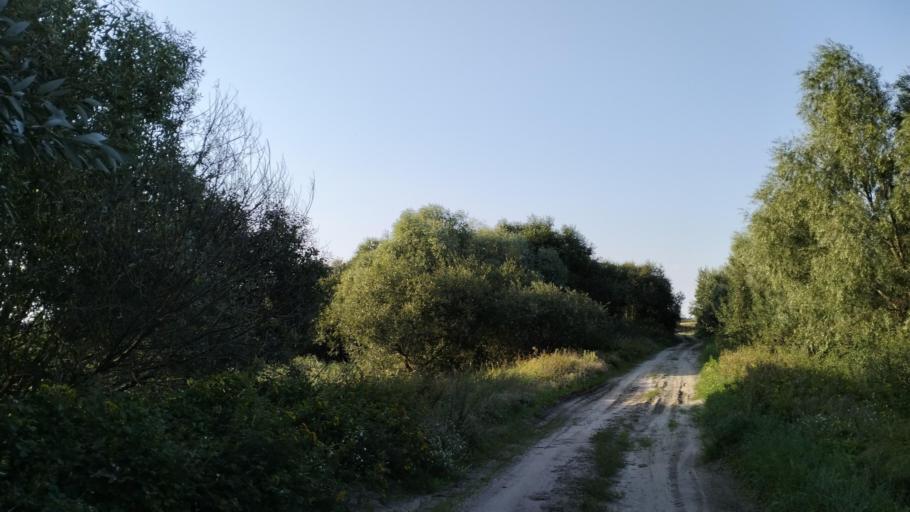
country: BY
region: Brest
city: Davyd-Haradok
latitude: 52.0289
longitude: 27.1949
